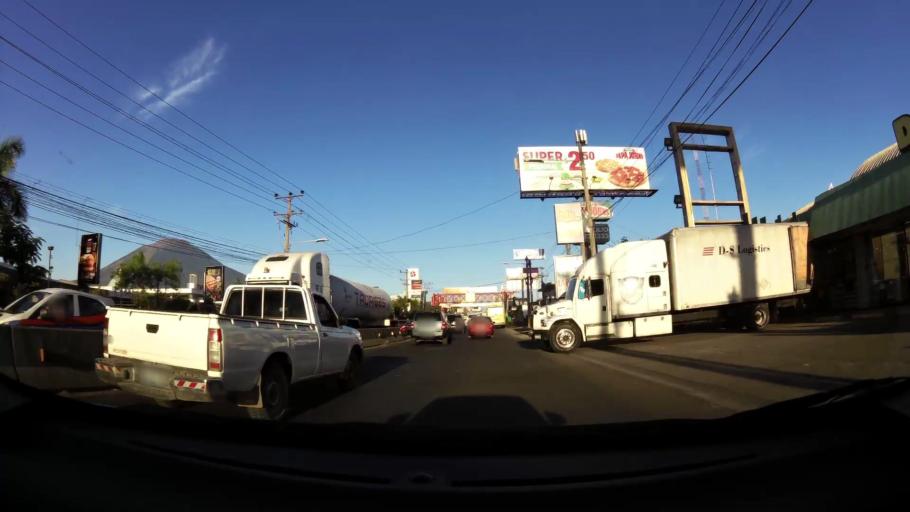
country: SV
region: San Miguel
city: San Miguel
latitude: 13.4622
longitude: -88.1644
